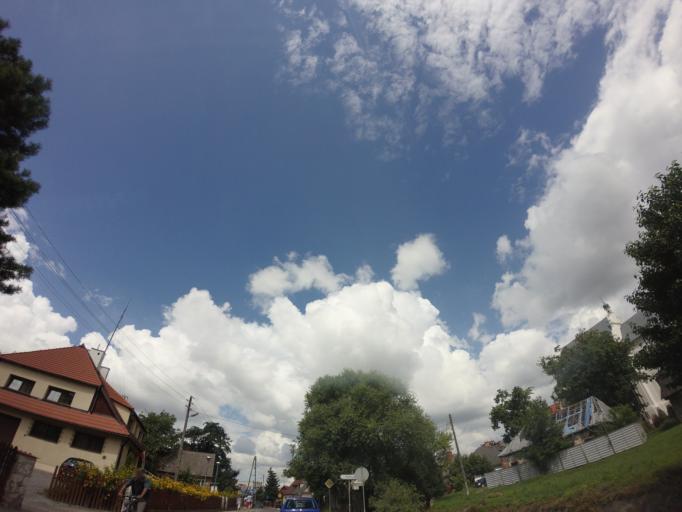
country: PL
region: Lublin Voivodeship
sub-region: Powiat pulawski
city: Kazimierz Dolny
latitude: 51.3205
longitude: 21.9489
